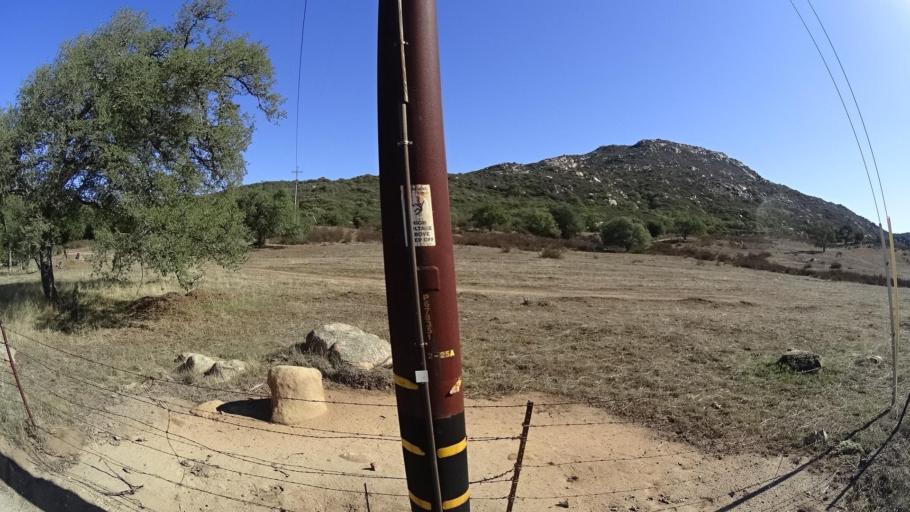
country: US
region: California
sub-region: San Diego County
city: Alpine
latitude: 32.7179
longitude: -116.7574
